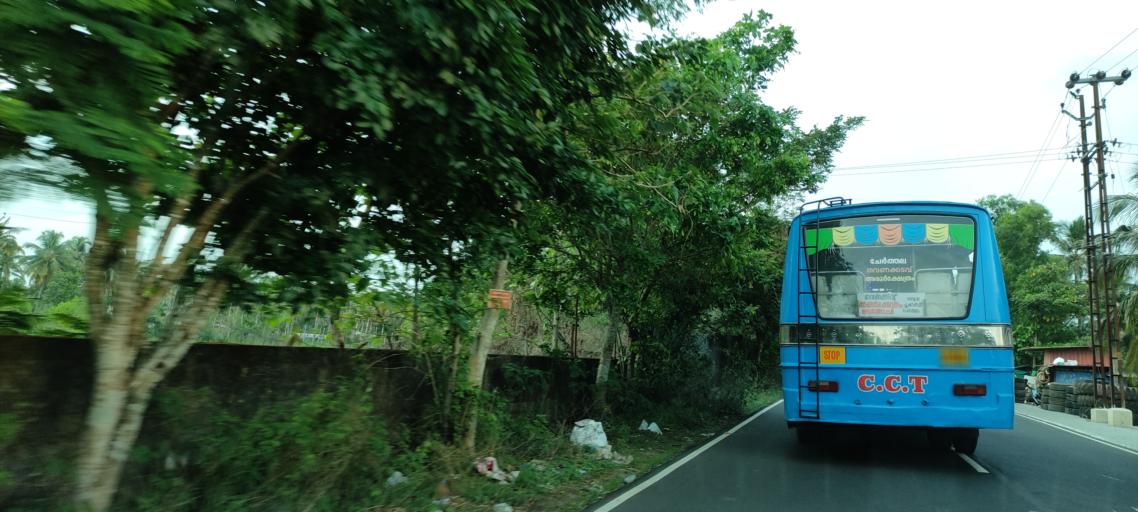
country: IN
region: Kerala
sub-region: Alappuzha
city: Kutiatodu
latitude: 9.7844
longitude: 76.3598
